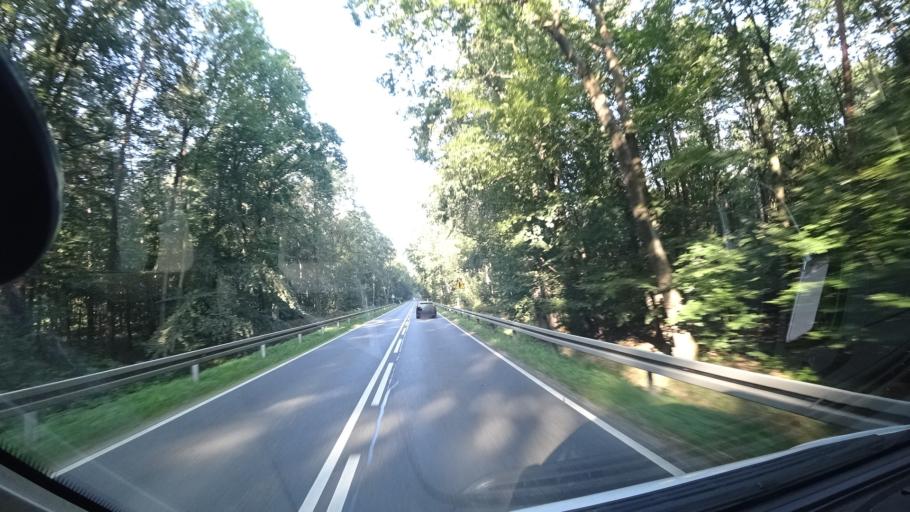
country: PL
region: Silesian Voivodeship
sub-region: Powiat gliwicki
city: Sosnicowice
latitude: 50.2794
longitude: 18.5070
